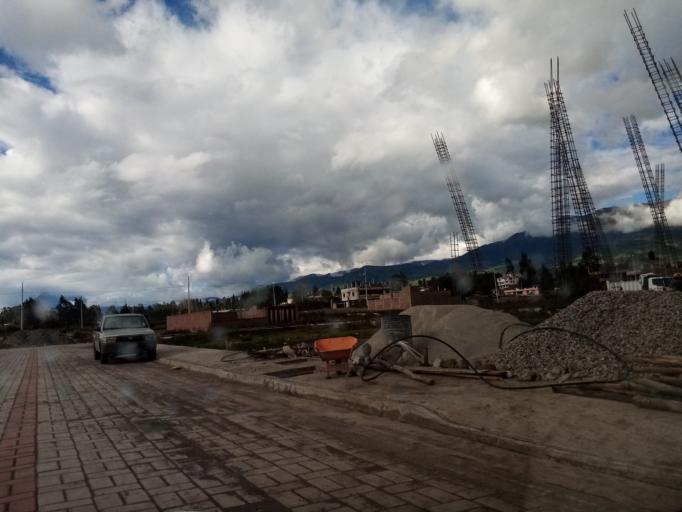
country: EC
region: Chimborazo
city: Riobamba
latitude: -1.6874
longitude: -78.6241
